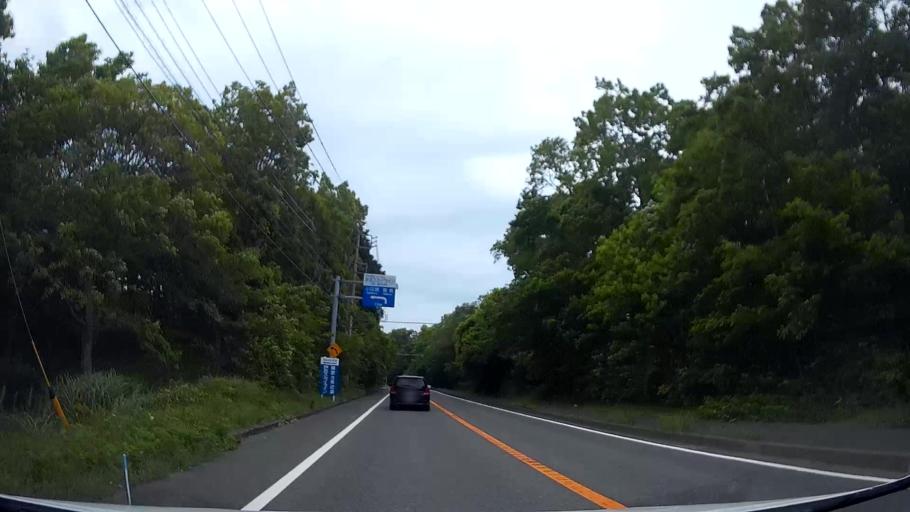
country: JP
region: Shizuoka
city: Ito
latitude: 34.8985
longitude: 139.1213
